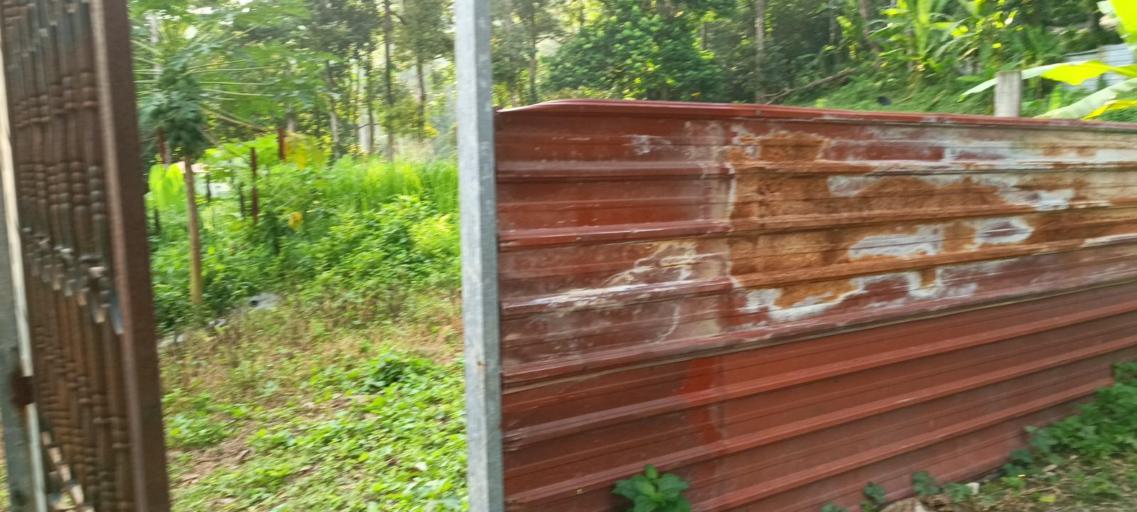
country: MY
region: Penang
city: Bukit Mertajam
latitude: 5.3746
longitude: 100.4752
